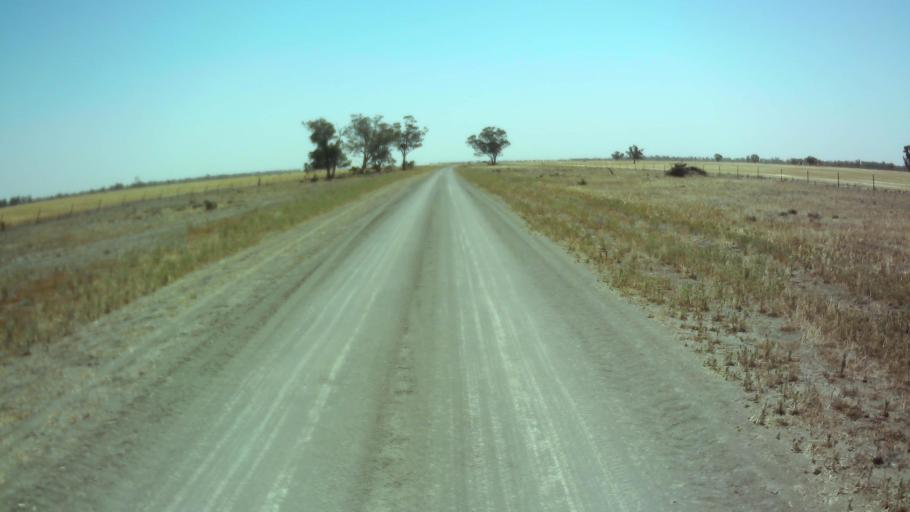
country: AU
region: New South Wales
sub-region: Weddin
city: Grenfell
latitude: -33.9966
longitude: 147.8745
